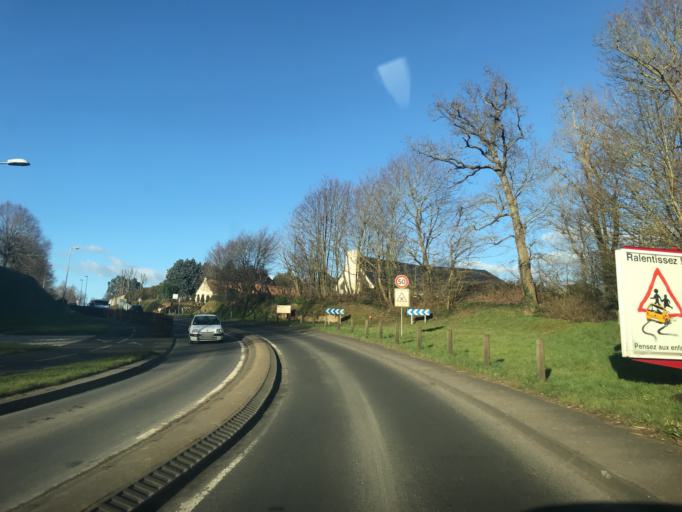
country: FR
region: Lower Normandy
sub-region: Departement du Calvados
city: Beuville
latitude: 49.2271
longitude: -0.3330
